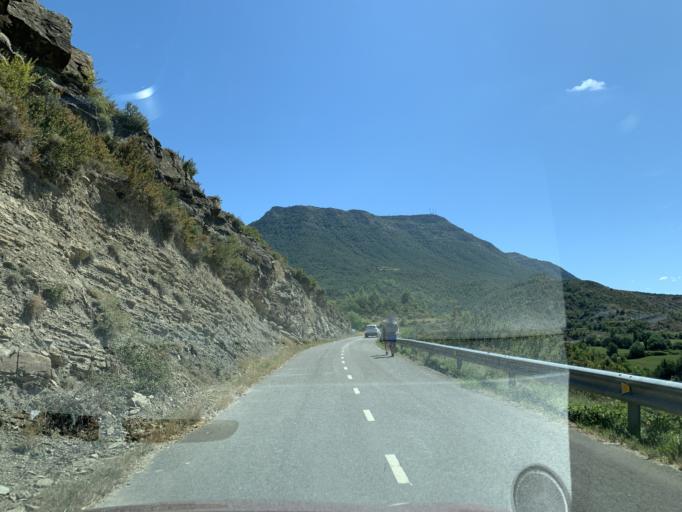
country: ES
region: Aragon
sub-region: Provincia de Huesca
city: Sabinanigo
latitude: 42.5209
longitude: -0.3243
